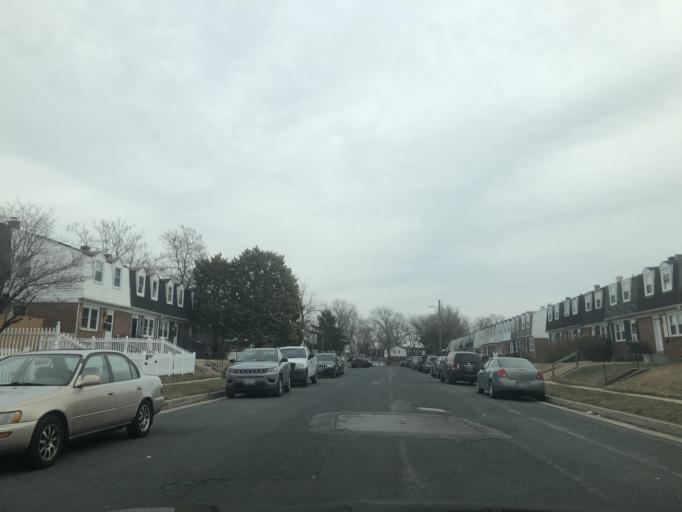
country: US
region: Maryland
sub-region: Baltimore County
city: Dundalk
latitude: 39.2614
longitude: -76.4951
